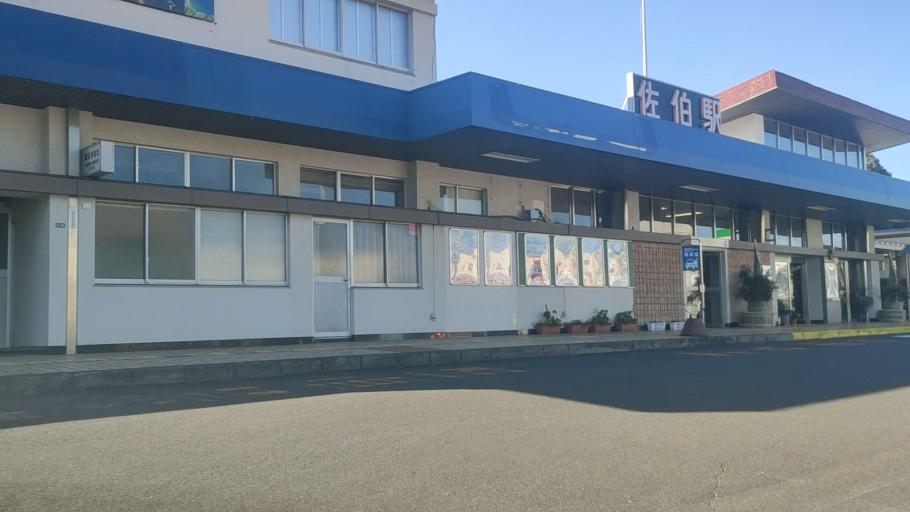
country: JP
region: Oita
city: Saiki
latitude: 32.9724
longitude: 131.9023
